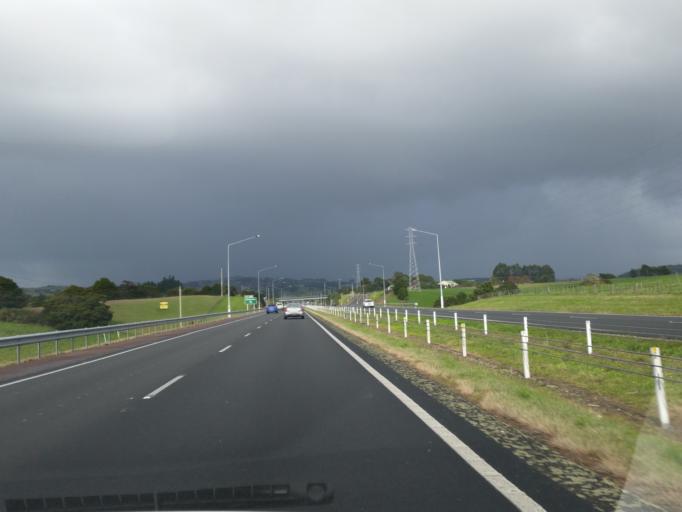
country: NZ
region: Auckland
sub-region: Auckland
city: Pukekohe East
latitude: -37.1381
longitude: 174.9665
